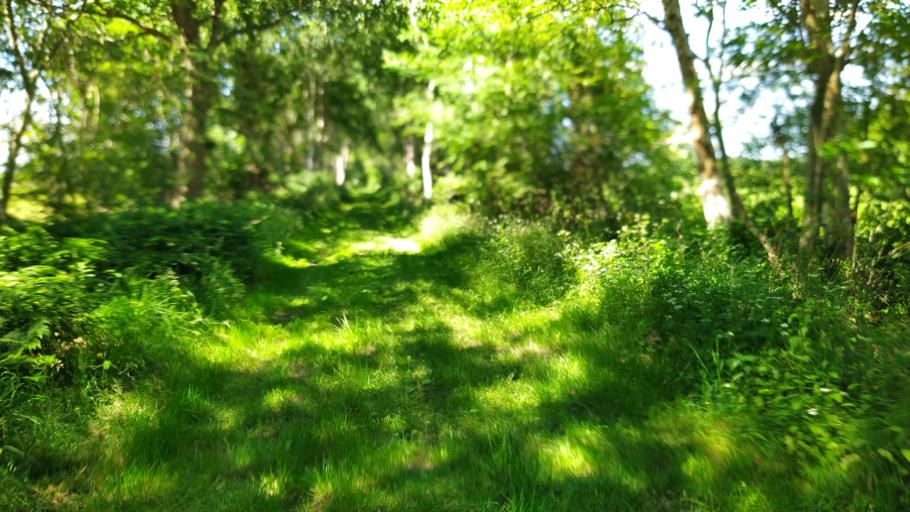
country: DE
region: Lower Saxony
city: Oldendorf
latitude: 53.5630
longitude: 9.2531
